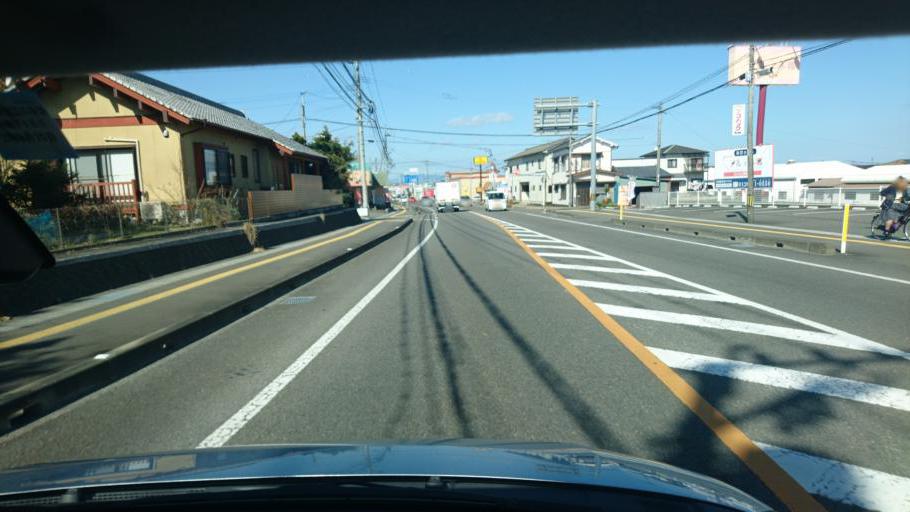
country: JP
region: Miyazaki
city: Miyazaki-shi
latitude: 31.8701
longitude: 131.4317
